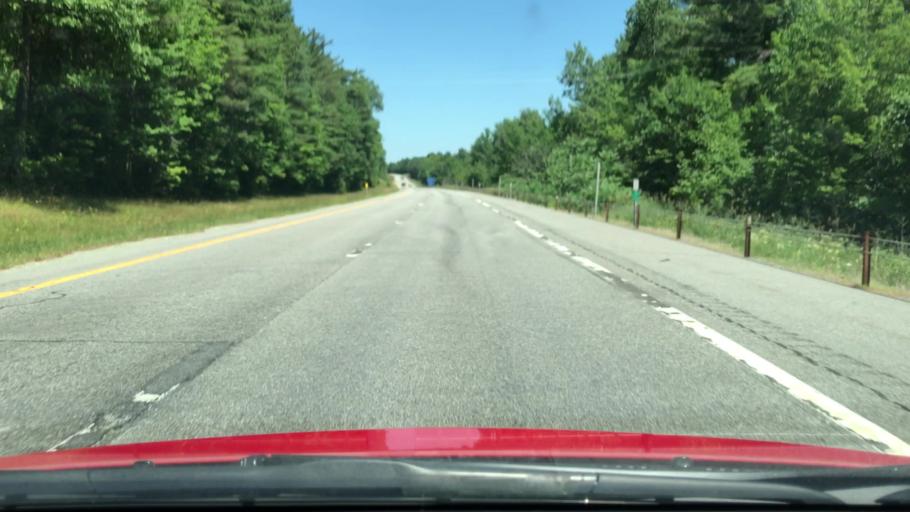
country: US
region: New York
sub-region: Essex County
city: Elizabethtown
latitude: 44.1403
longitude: -73.5844
